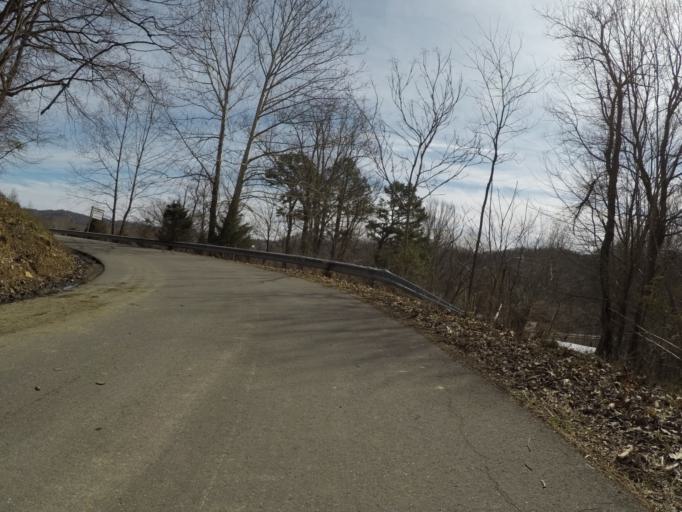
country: US
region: West Virginia
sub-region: Wayne County
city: Ceredo
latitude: 38.3734
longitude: -82.5421
